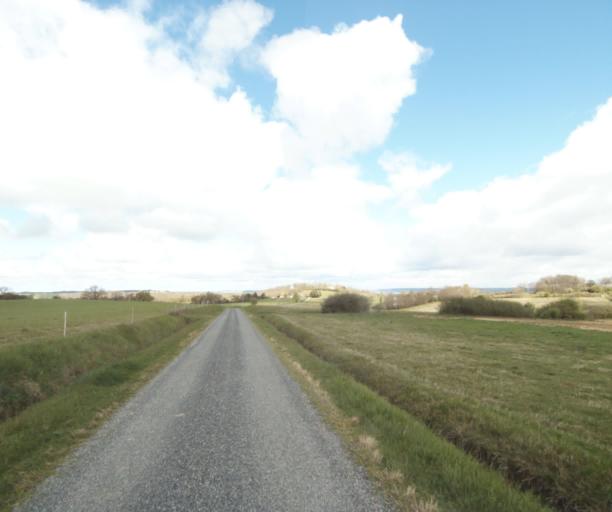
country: FR
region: Midi-Pyrenees
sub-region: Departement de l'Ariege
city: Saverdun
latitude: 43.1816
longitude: 1.5789
